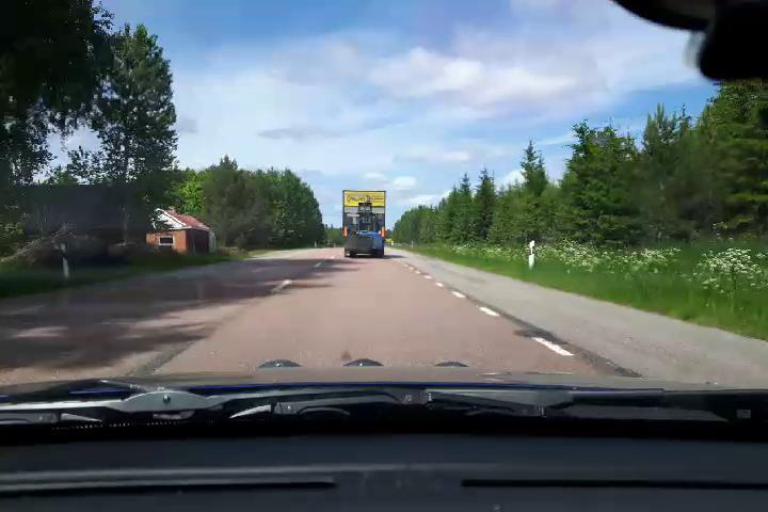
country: SE
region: Uppsala
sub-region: Osthammars Kommun
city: Bjorklinge
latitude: 60.1515
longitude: 17.4929
